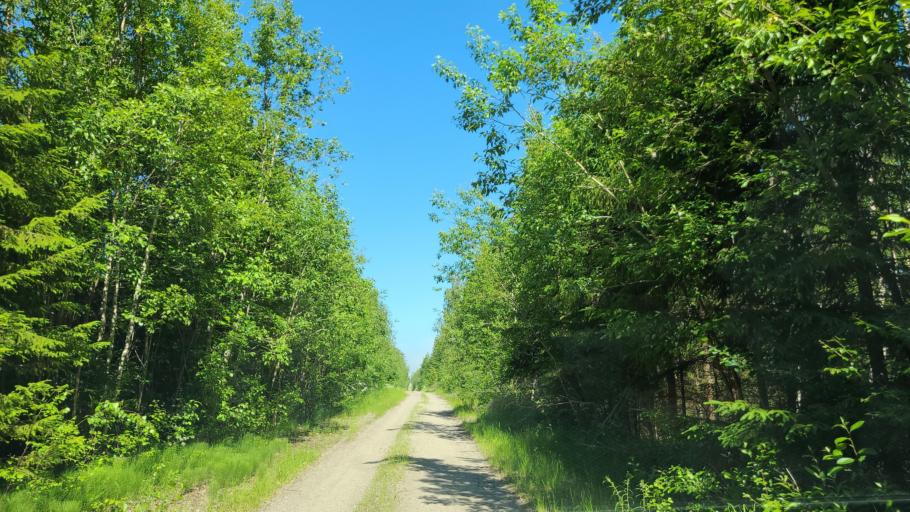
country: SE
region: Vaesternorrland
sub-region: OErnskoeldsviks Kommun
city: Husum
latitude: 63.4244
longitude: 19.2252
